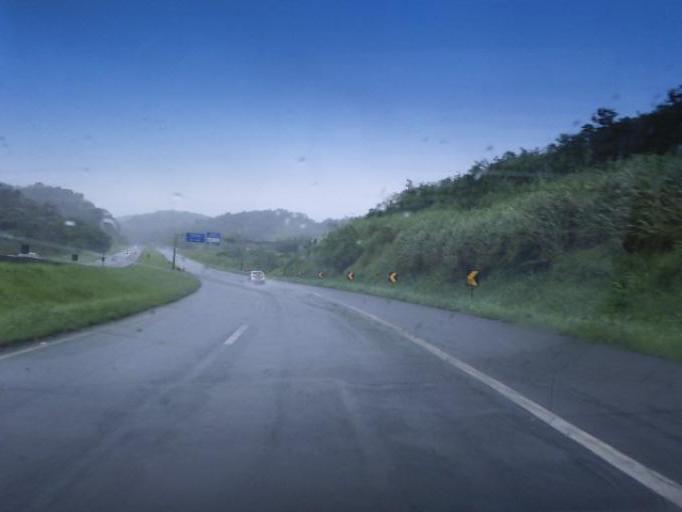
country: BR
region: Sao Paulo
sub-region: Juquia
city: Juquia
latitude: -24.3985
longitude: -47.7309
